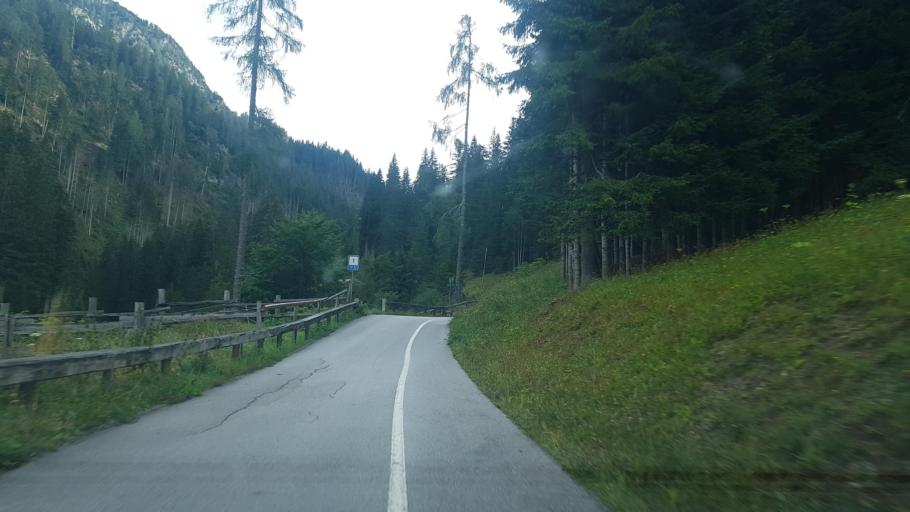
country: IT
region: Veneto
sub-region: Provincia di Belluno
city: Granvilla
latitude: 46.5749
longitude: 12.7246
